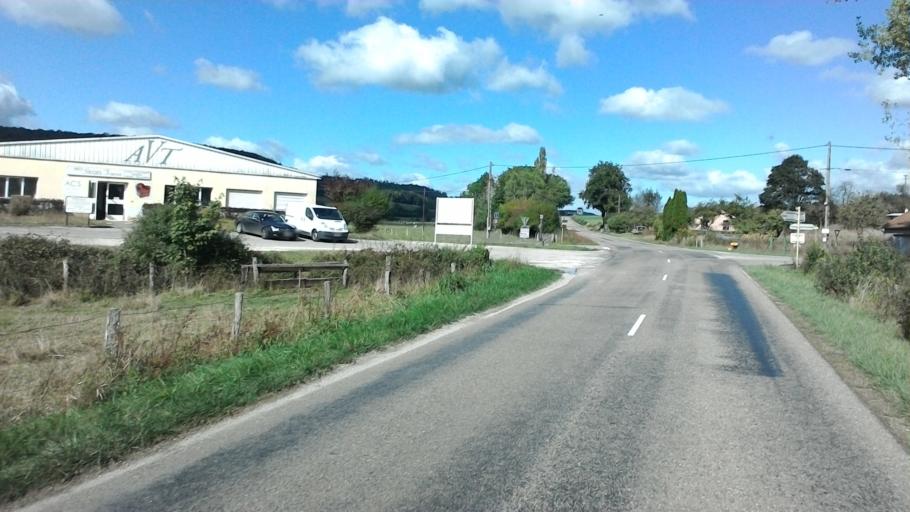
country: FR
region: Lorraine
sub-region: Departement des Vosges
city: Neufchateau
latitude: 48.3691
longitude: 5.6806
